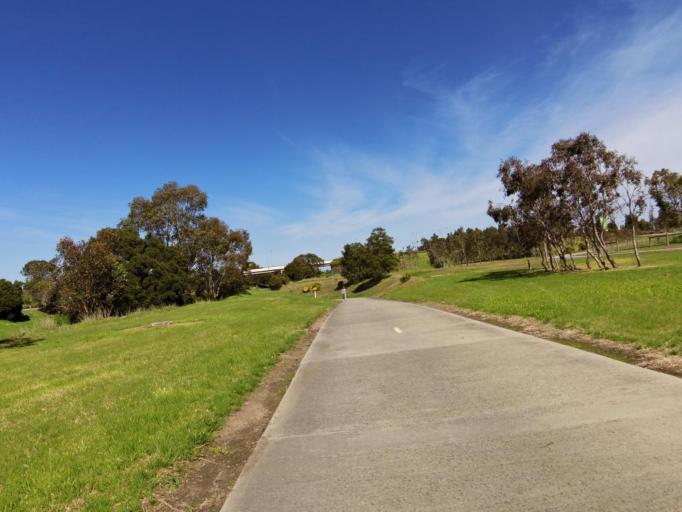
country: AU
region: Victoria
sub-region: Greater Dandenong
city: Dandenong
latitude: -37.9987
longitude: 145.1940
